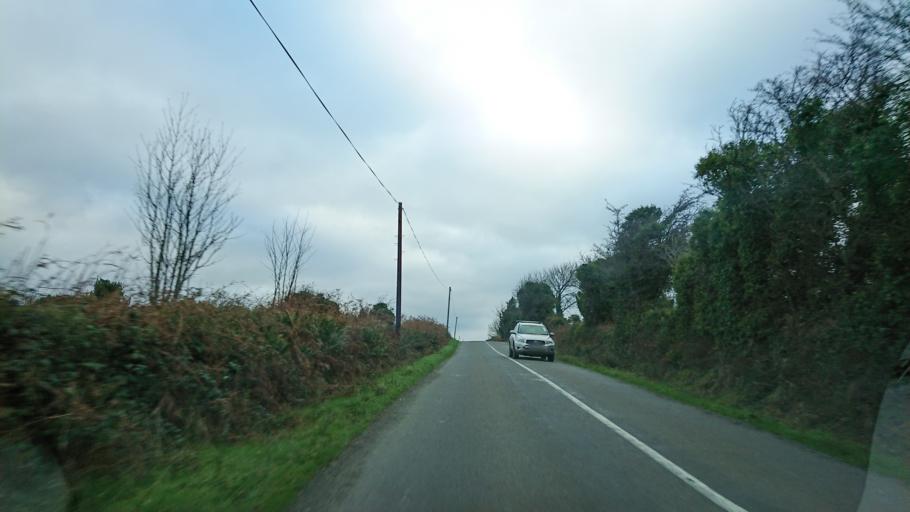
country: IE
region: Munster
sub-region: South Tipperary
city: Cluain Meala
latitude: 52.3200
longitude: -7.5597
